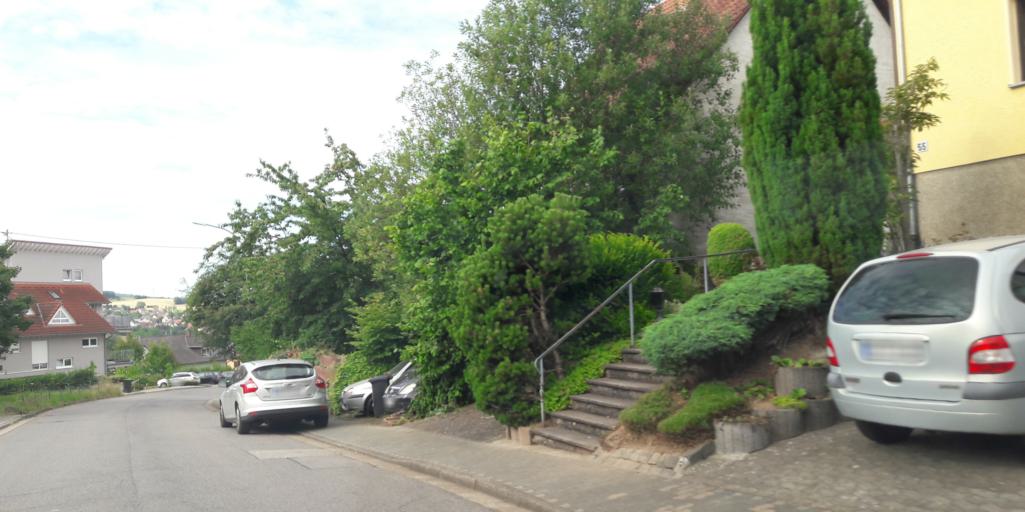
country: DE
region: Saarland
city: Puttlingen
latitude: 49.3098
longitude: 6.9015
